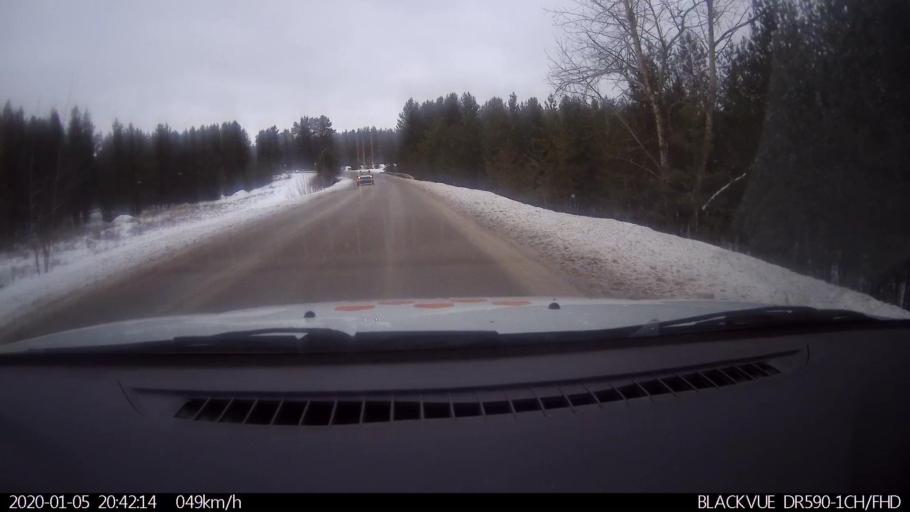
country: RU
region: Nizjnij Novgorod
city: Lukino
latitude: 56.3976
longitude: 43.7298
